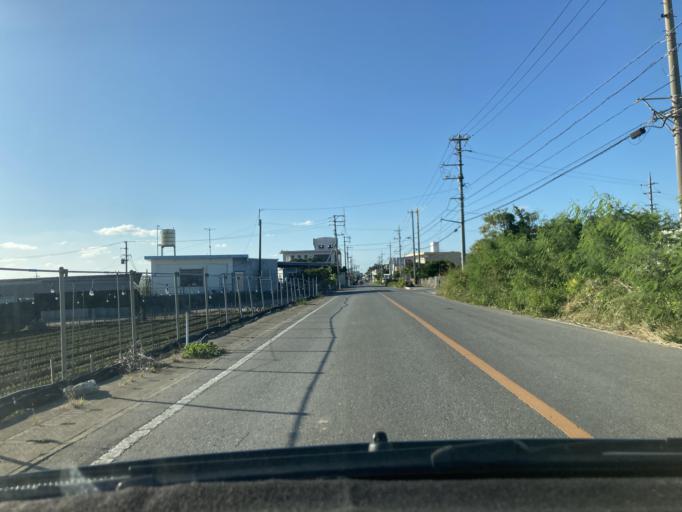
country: JP
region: Okinawa
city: Itoman
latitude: 26.1028
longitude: 127.6699
